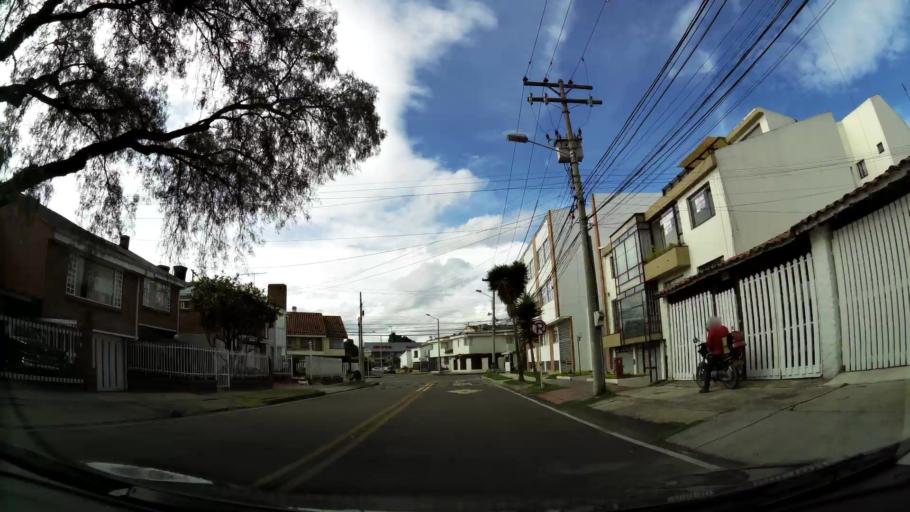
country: CO
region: Bogota D.C.
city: Barrio San Luis
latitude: 4.7116
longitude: -74.0751
